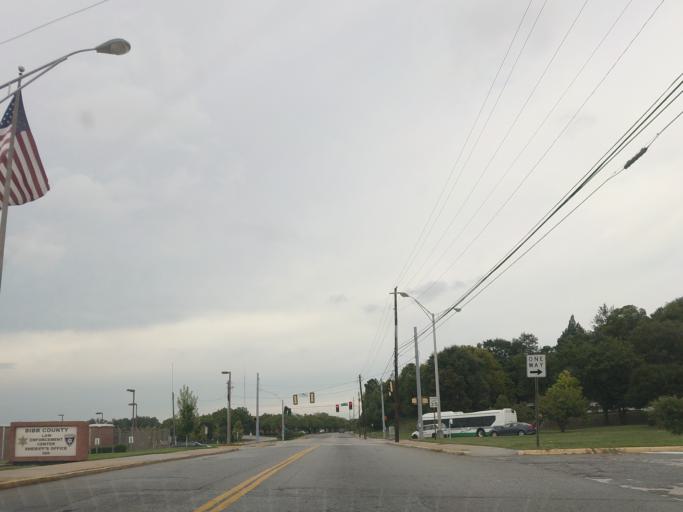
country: US
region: Georgia
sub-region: Bibb County
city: Macon
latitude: 32.8298
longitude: -83.6370
